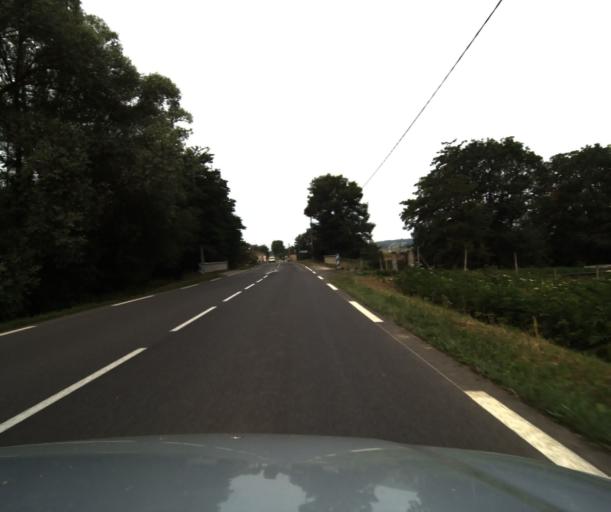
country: FR
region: Midi-Pyrenees
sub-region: Departement du Gers
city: Mielan
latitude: 43.4264
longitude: 0.2928
